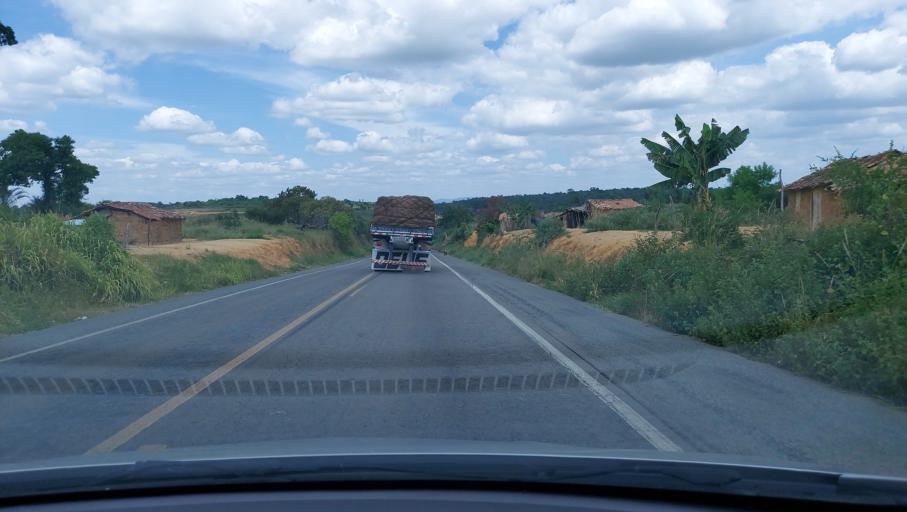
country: BR
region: Bahia
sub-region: Ruy Barbosa
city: Terra Nova
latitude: -12.4424
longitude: -40.7824
